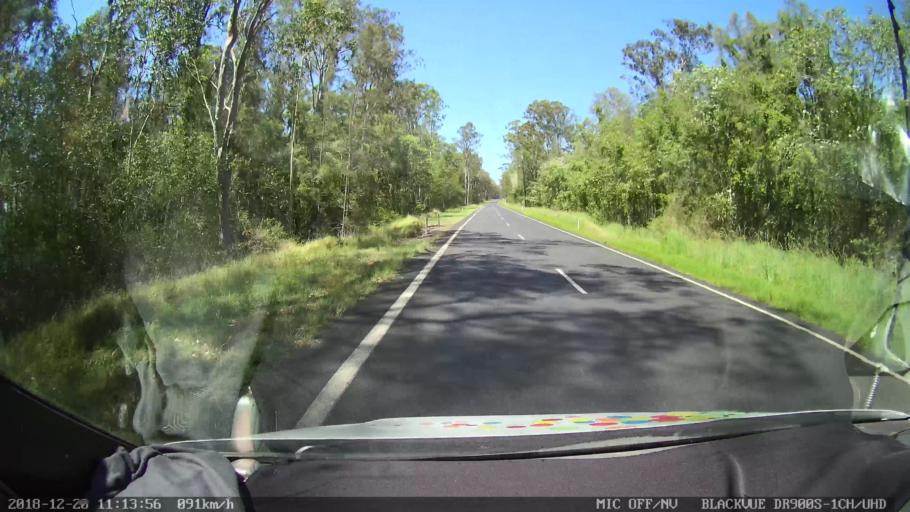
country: AU
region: New South Wales
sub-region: Richmond Valley
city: Casino
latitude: -28.9943
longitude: 153.0113
